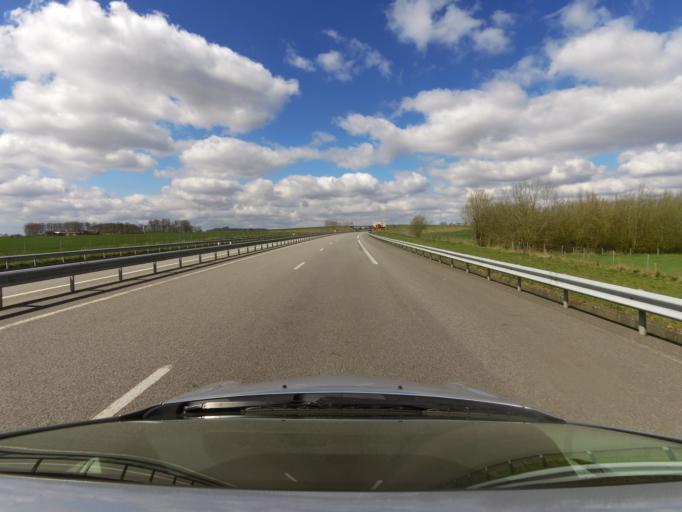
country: FR
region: Haute-Normandie
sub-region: Departement de la Seine-Maritime
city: Limesy
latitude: 49.6467
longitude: 0.9624
